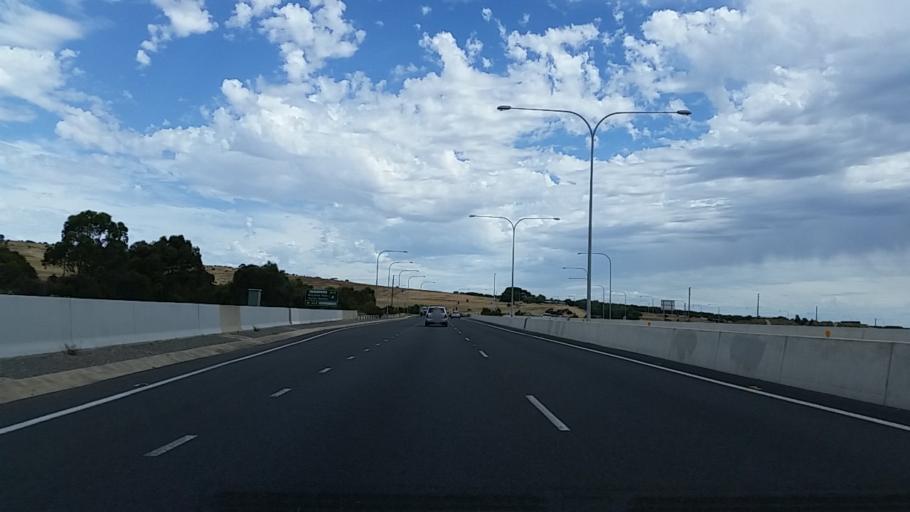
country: AU
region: South Australia
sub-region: Onkaparinga
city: Noarlunga Downs
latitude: -35.1628
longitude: 138.5079
